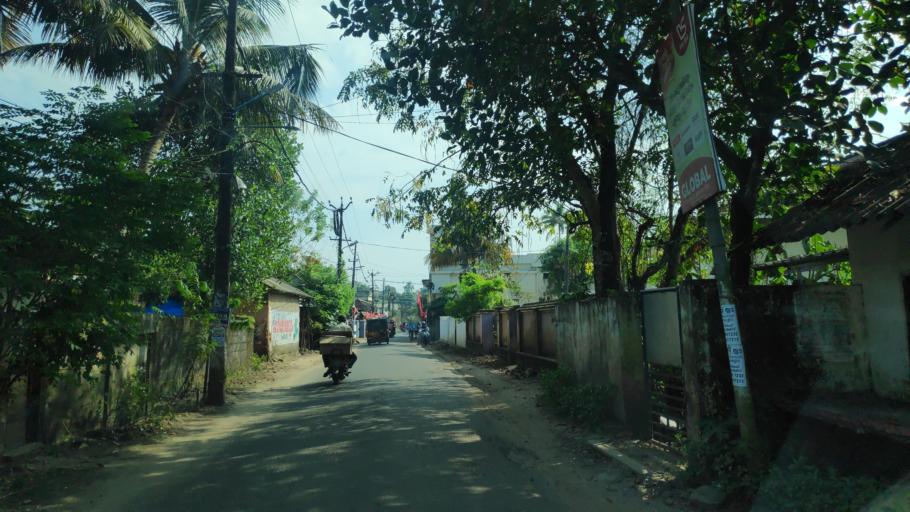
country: IN
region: Kerala
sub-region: Alappuzha
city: Alleppey
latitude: 9.5052
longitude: 76.3207
